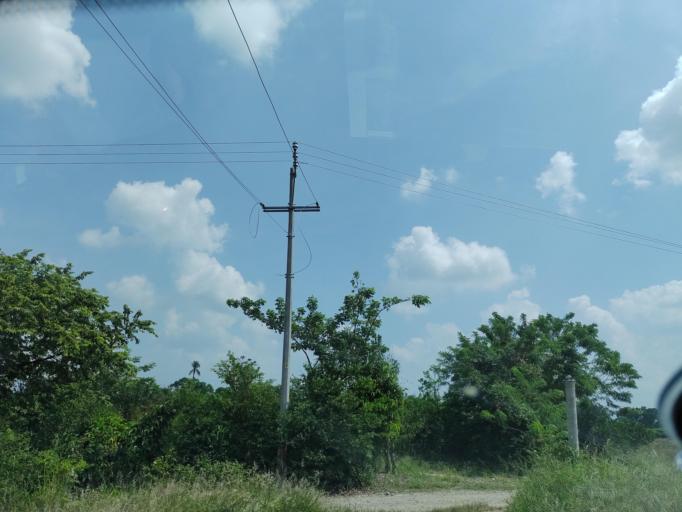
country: MX
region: Veracruz
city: Martinez de la Torre
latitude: 20.0883
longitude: -97.0380
